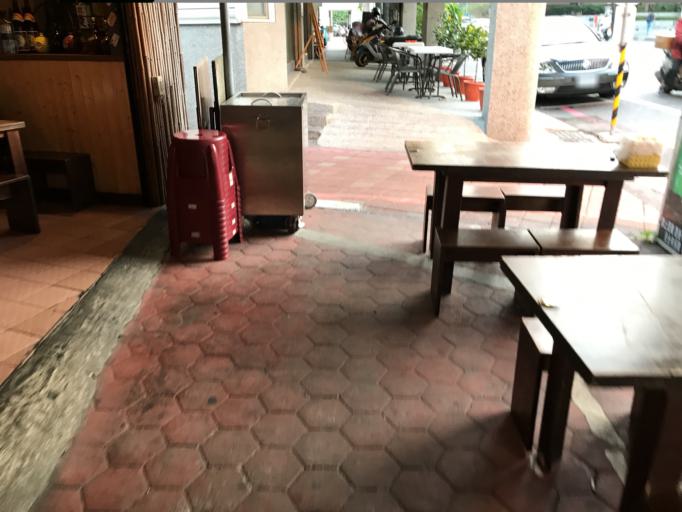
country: TW
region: Taiwan
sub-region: Tainan
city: Tainan
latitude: 22.9940
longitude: 120.2054
